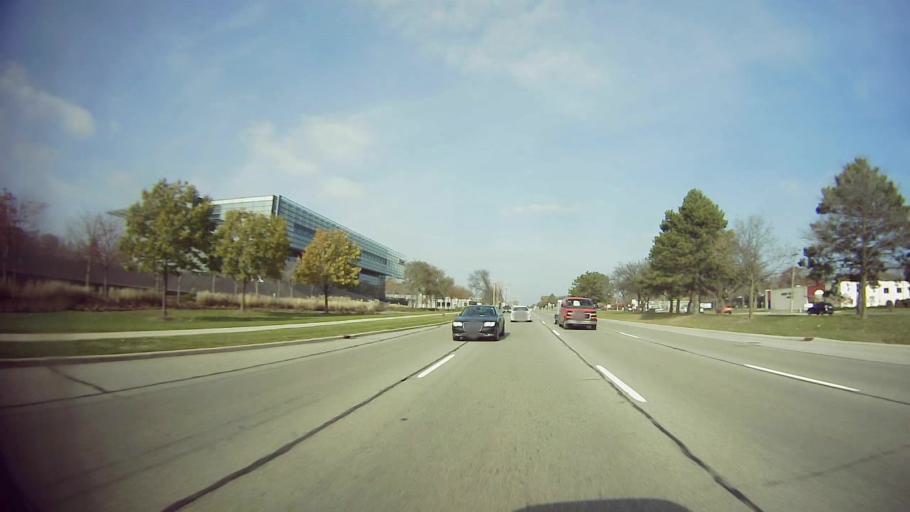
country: US
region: Michigan
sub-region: Oakland County
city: Southfield
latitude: 42.4519
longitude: -83.2785
